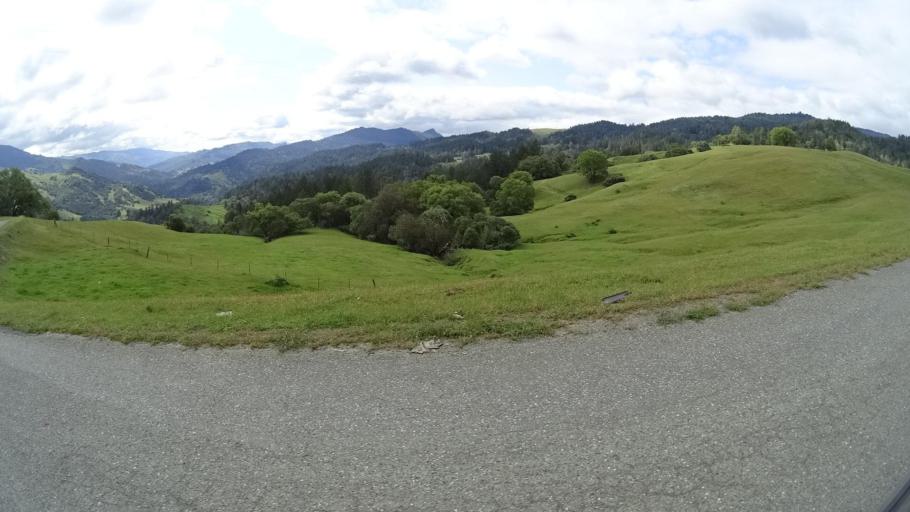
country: US
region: California
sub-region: Humboldt County
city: Redway
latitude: 40.1586
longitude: -123.6194
